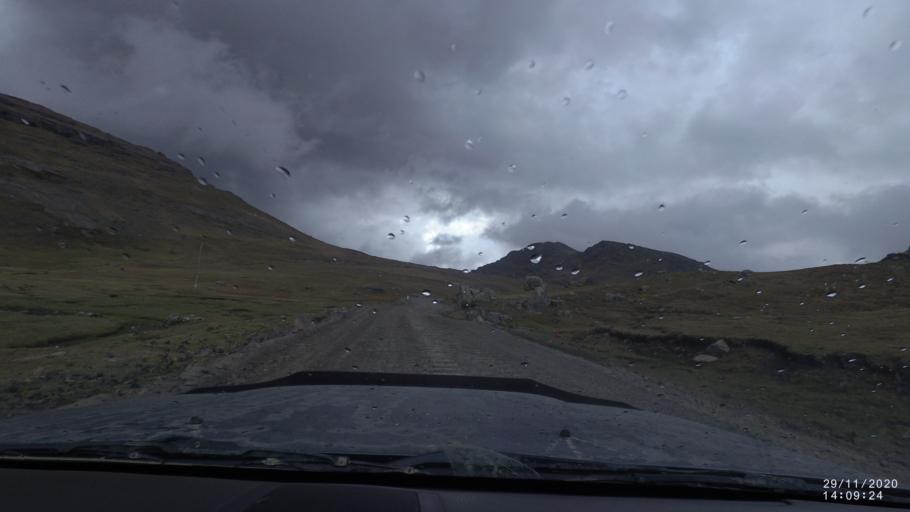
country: BO
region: Cochabamba
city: Sipe Sipe
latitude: -17.2269
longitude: -66.3856
